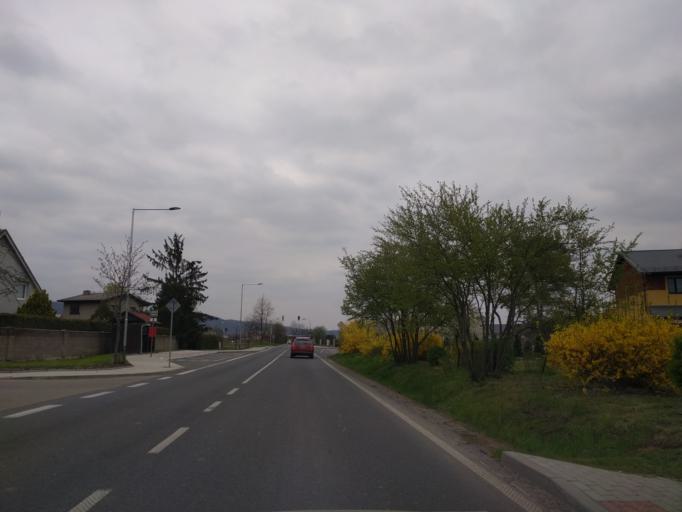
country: CZ
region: Central Bohemia
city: Revnice
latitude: 49.9205
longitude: 14.2504
